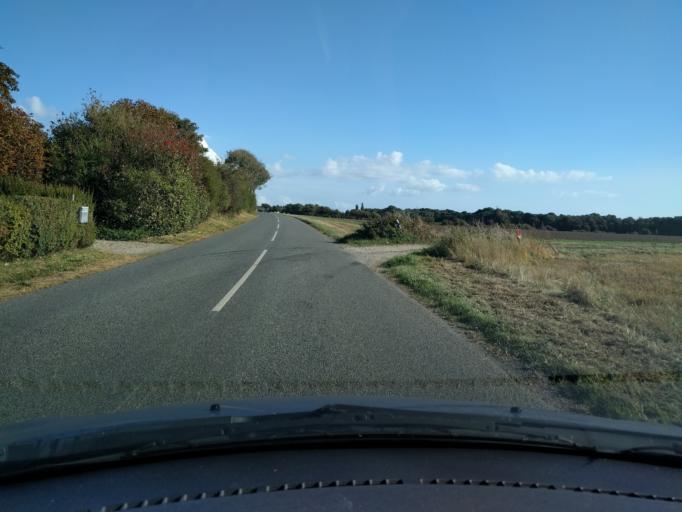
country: DK
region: South Denmark
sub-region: Assens Kommune
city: Harby
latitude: 55.1543
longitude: 10.0081
